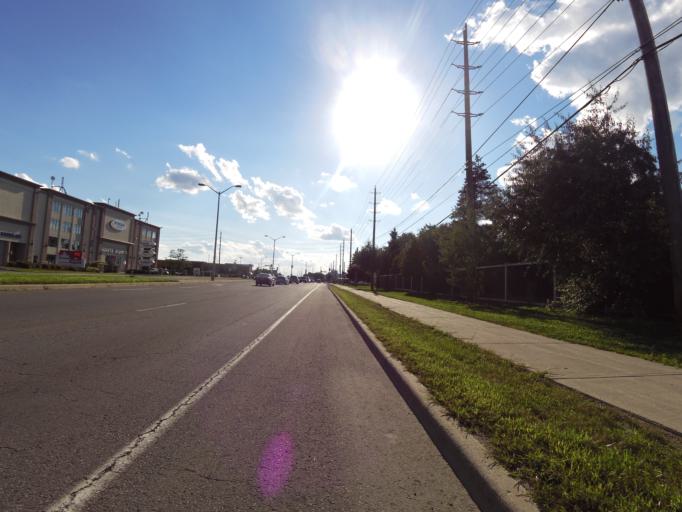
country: CA
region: Quebec
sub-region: Outaouais
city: Gatineau
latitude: 45.4599
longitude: -75.4914
